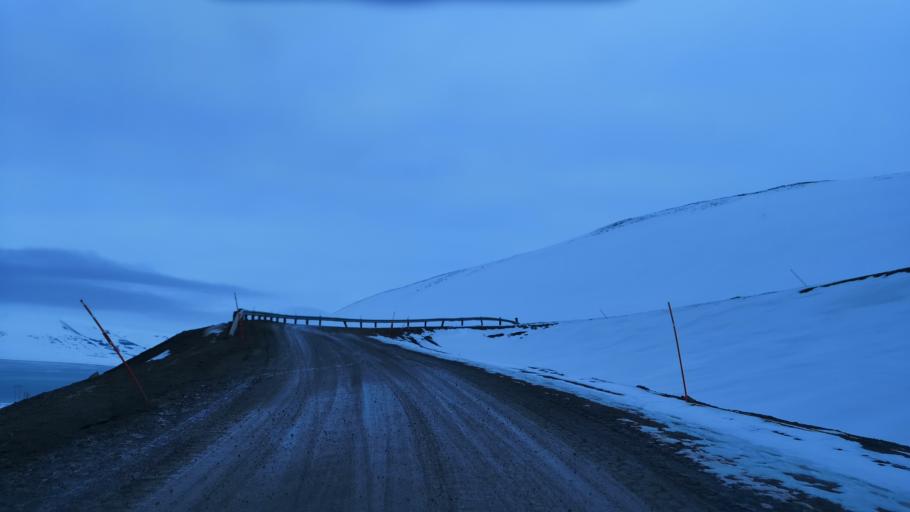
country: SJ
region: Svalbard
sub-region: Spitsbergen
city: Longyearbyen
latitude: 78.2372
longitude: 15.4984
